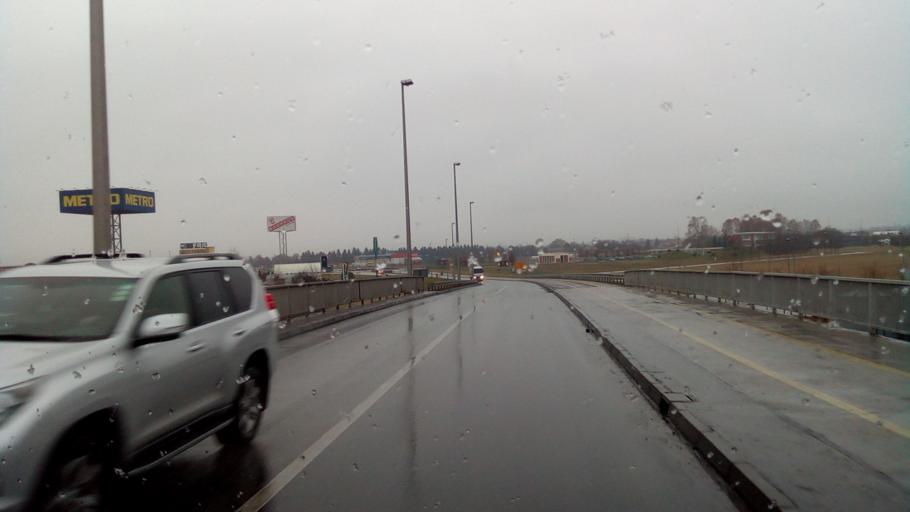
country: HR
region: Varazdinska
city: Varazdin
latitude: 46.2952
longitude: 16.3520
